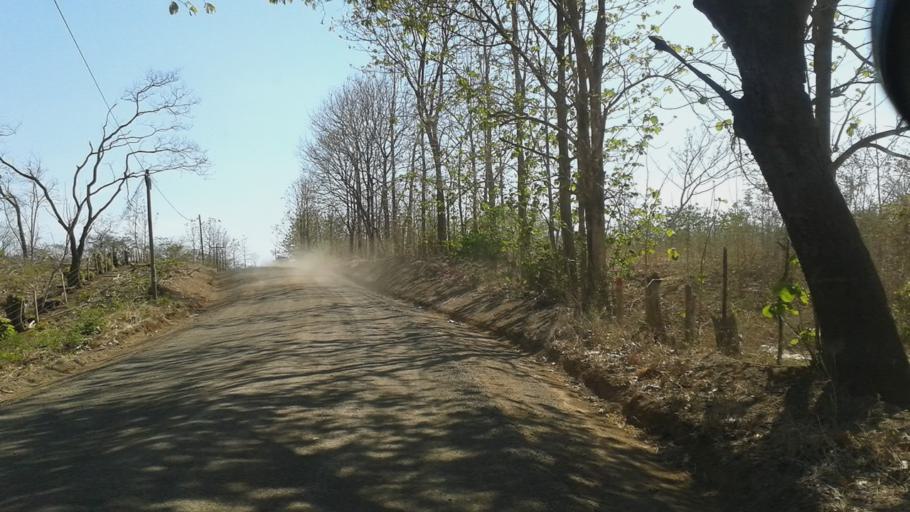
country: CR
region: Guanacaste
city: Santa Cruz
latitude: 10.1747
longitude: -85.7800
